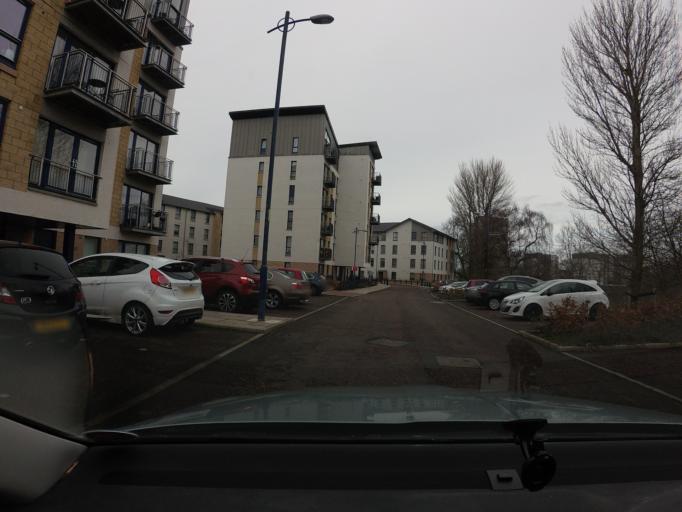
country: GB
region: Scotland
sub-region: South Lanarkshire
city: Rutherglen
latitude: 55.8421
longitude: -4.2377
